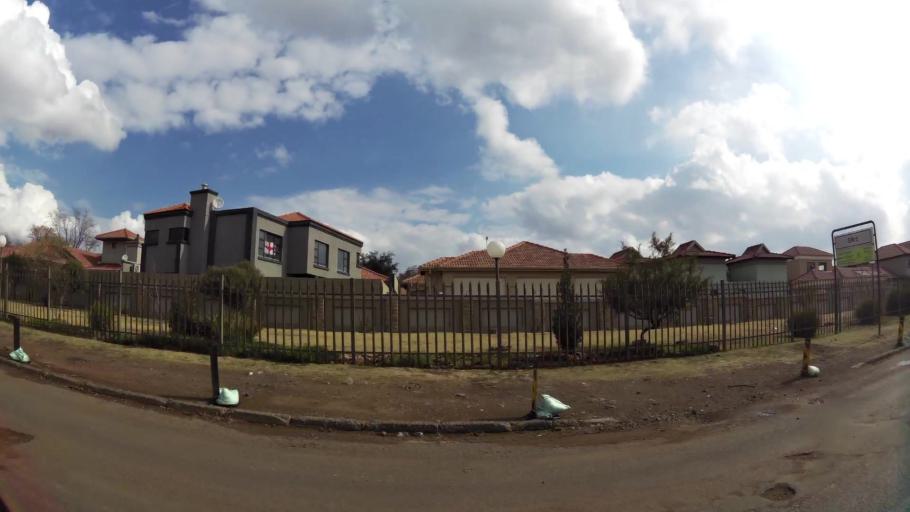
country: ZA
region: Gauteng
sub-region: Sedibeng District Municipality
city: Vanderbijlpark
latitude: -26.7348
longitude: 27.8377
